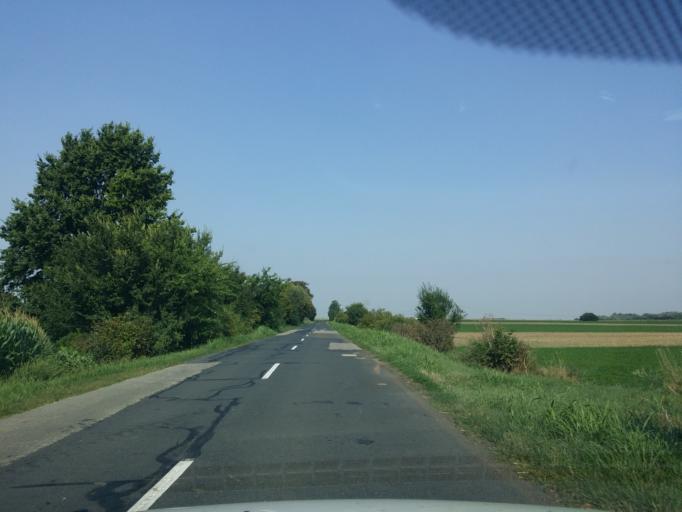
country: HU
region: Fejer
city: Mezofalva
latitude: 46.9479
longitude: 18.7345
